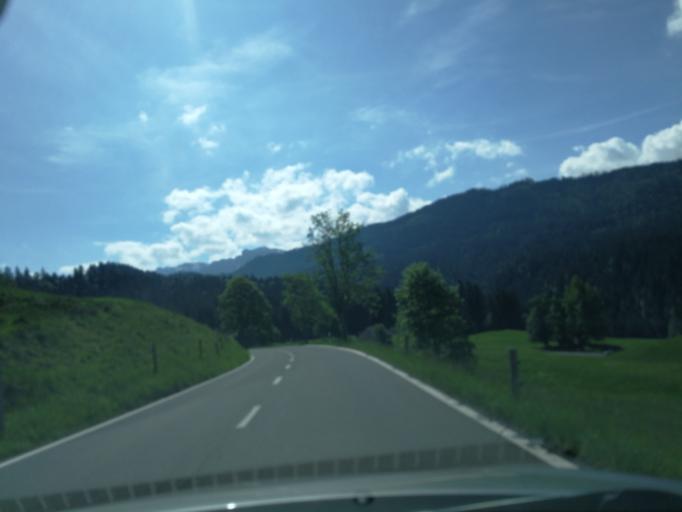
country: CH
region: Bern
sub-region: Emmental District
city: Eggiwil
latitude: 46.8248
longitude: 7.7849
